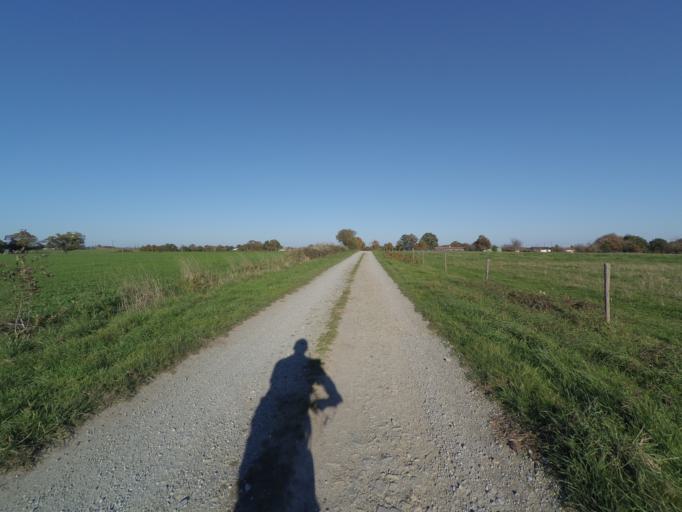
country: FR
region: Pays de la Loire
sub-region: Departement de la Loire-Atlantique
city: Remouille
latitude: 47.0248
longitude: -1.3928
